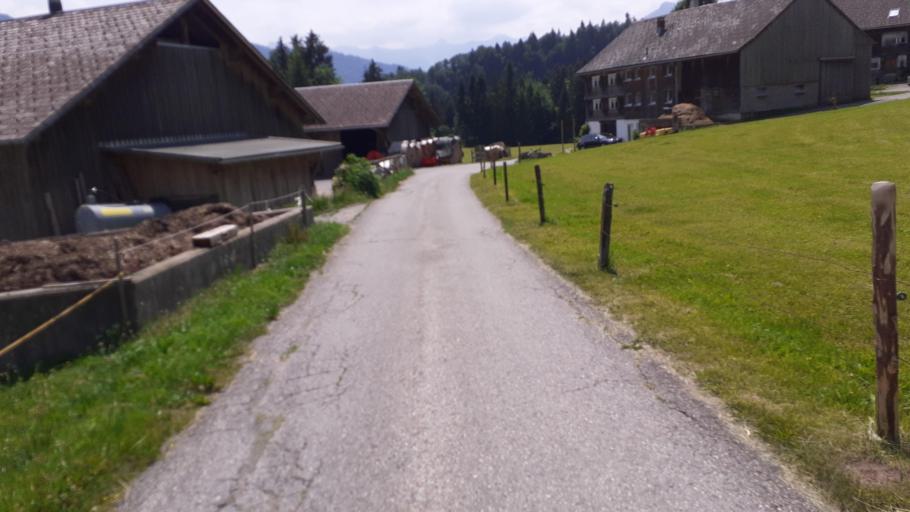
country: AT
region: Vorarlberg
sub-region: Politischer Bezirk Bregenz
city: Egg
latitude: 47.4375
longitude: 9.8840
